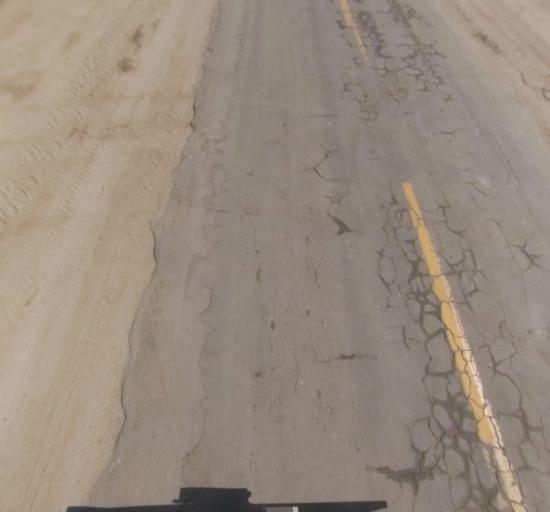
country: US
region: California
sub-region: Madera County
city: Parkwood
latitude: 36.8813
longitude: -120.1557
